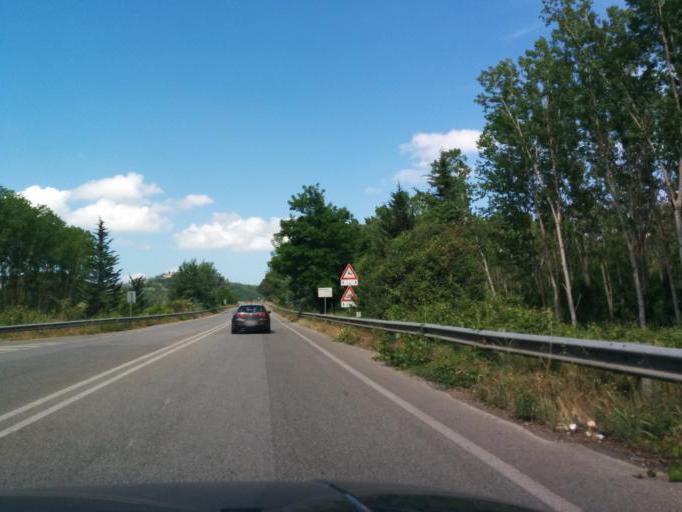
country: IT
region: Tuscany
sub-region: Provincia di Siena
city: Poggibonsi
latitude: 43.4592
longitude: 11.1051
